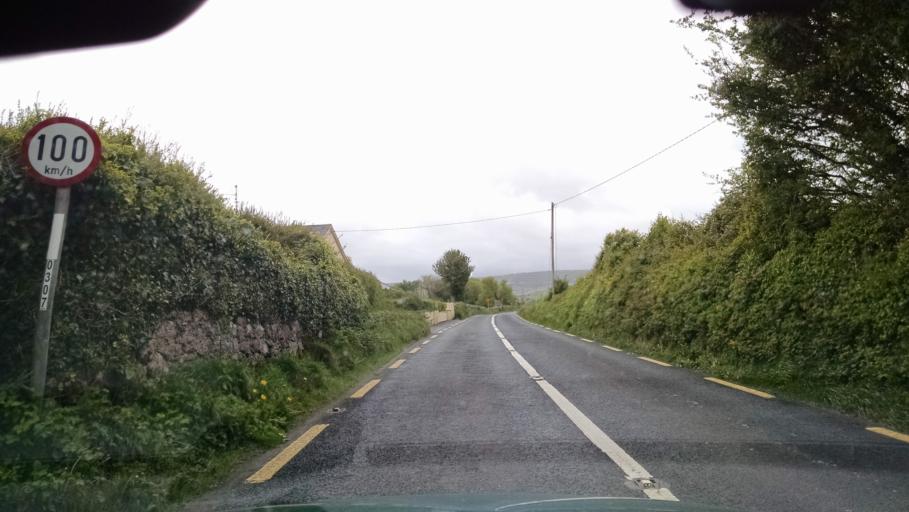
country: IE
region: Connaught
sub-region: County Galway
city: Bearna
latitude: 53.1055
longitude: -9.1567
